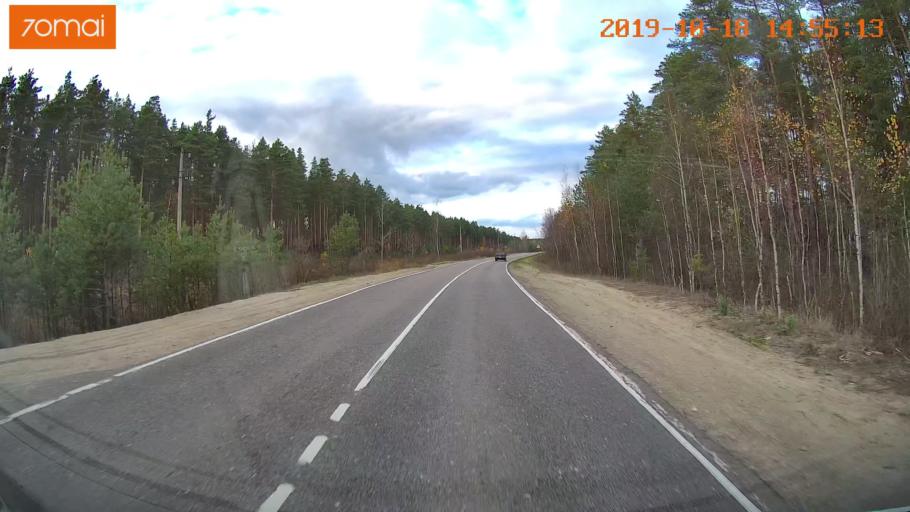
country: RU
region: Vladimir
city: Kurlovo
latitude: 55.4489
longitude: 40.5886
